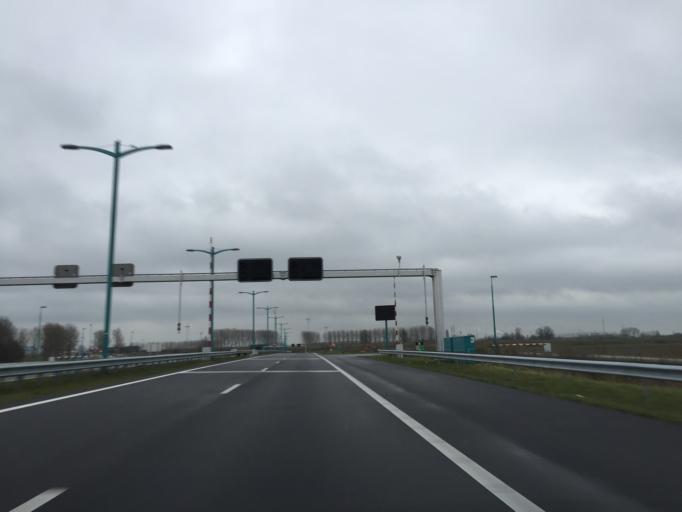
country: NL
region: Zeeland
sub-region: Gemeente Terneuzen
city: Sluiskil
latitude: 51.2928
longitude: 3.8198
